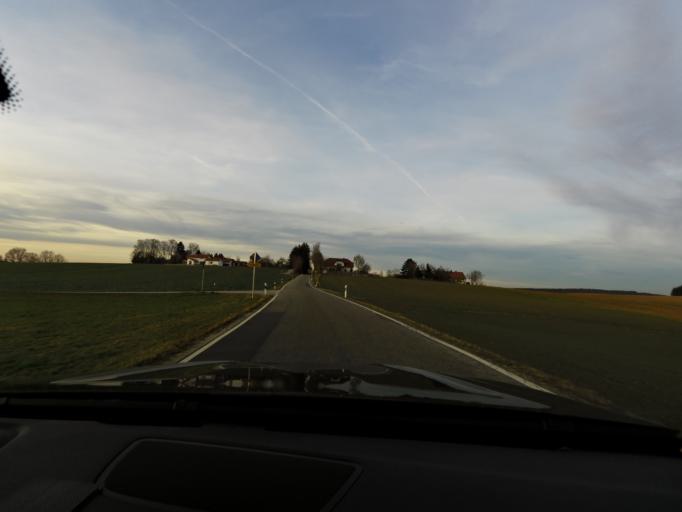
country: DE
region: Bavaria
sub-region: Lower Bavaria
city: Vilsheim
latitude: 48.4697
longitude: 12.1078
